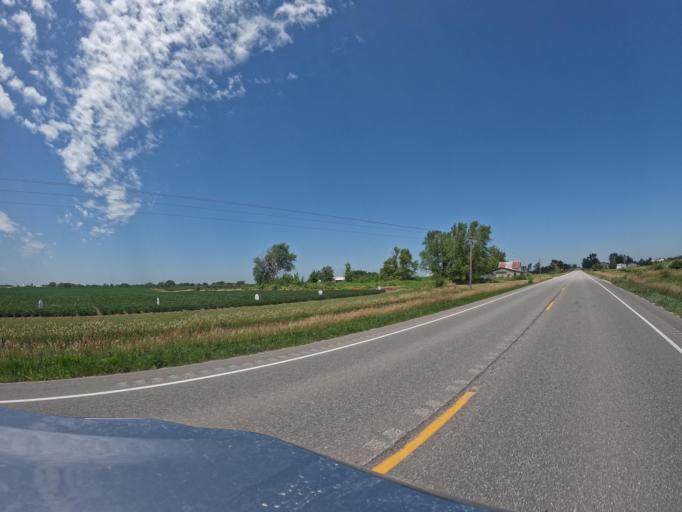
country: US
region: Iowa
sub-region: Keokuk County
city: Sigourney
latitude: 41.4250
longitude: -92.3547
